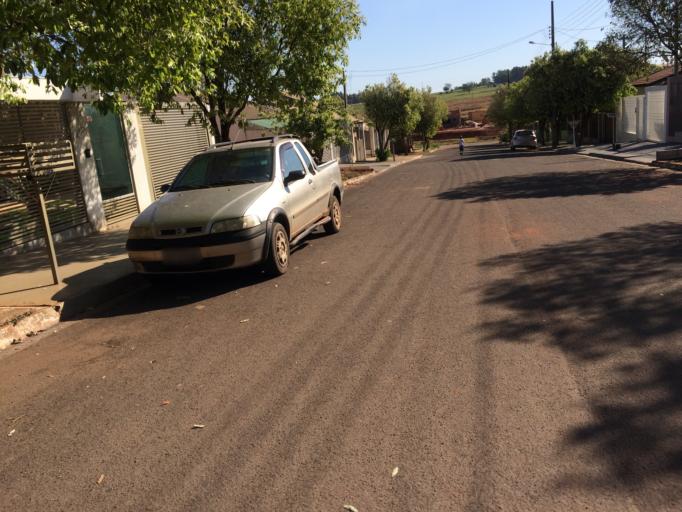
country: BR
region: Parana
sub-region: Cianorte
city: Cianorte
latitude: -23.5389
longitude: -52.5936
